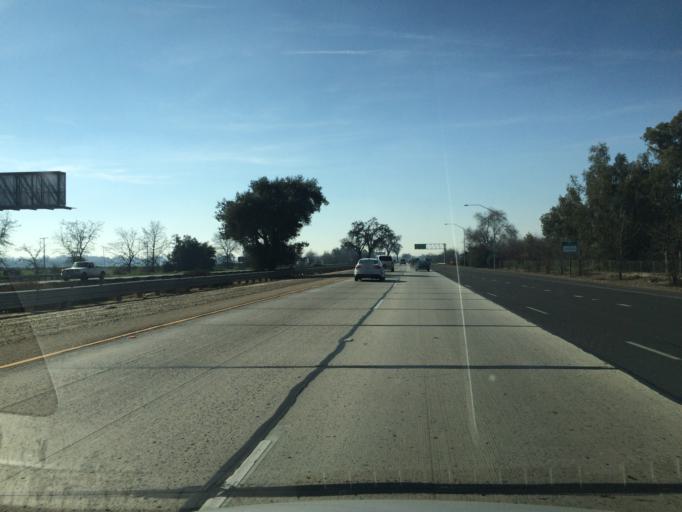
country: US
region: California
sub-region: Tulare County
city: Visalia
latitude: 36.3274
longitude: -119.3537
